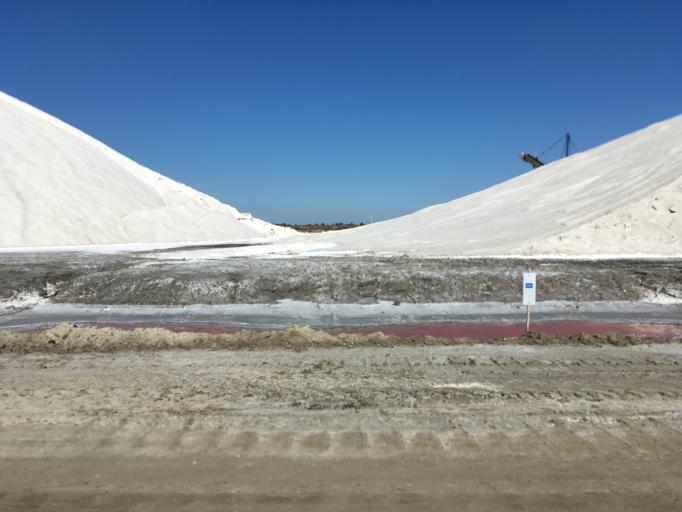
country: FR
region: Languedoc-Roussillon
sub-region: Departement du Gard
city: Aigues-Mortes
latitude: 43.5471
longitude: 4.1839
